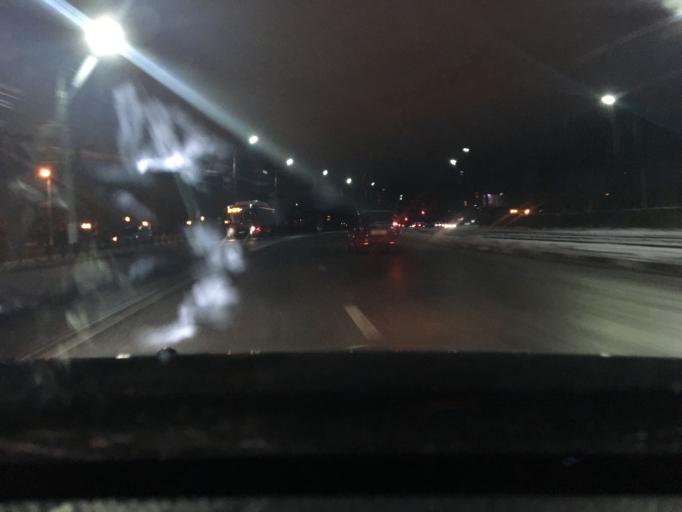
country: RU
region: Tula
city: Mendeleyevskiy
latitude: 54.1651
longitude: 37.5873
